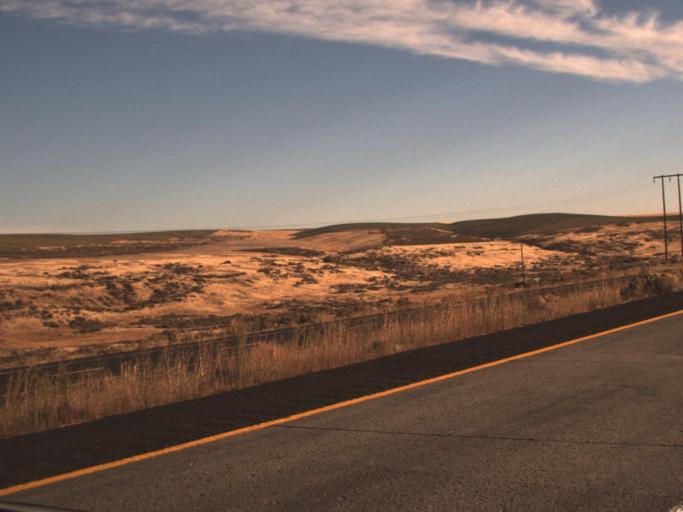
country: US
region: Washington
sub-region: Adams County
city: Ritzville
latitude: 47.0471
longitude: -118.4411
